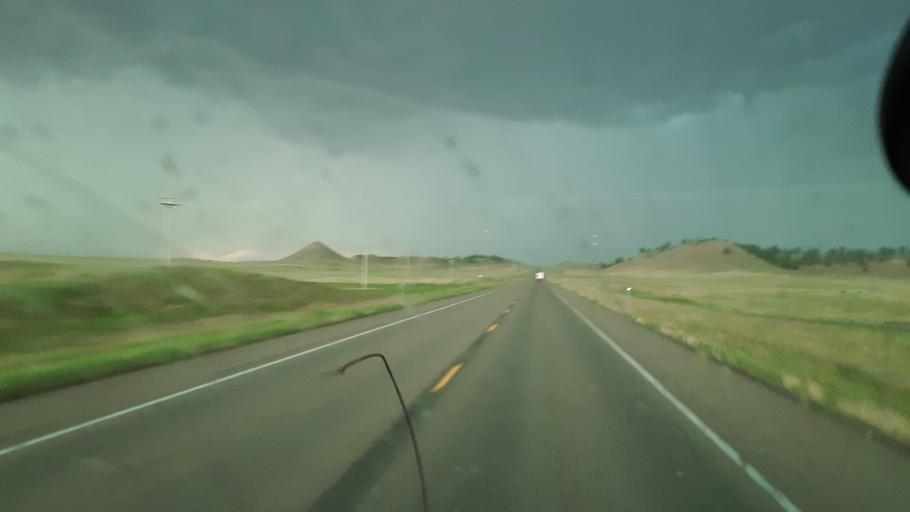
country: US
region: Montana
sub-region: Powder River County
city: Broadus
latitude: 45.4702
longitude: -105.4814
